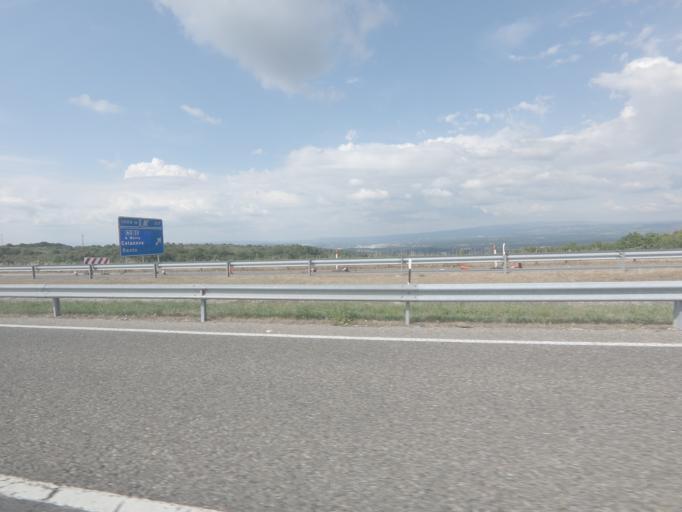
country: ES
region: Galicia
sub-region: Provincia de Ourense
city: Taboadela
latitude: 42.2373
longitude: -7.8567
